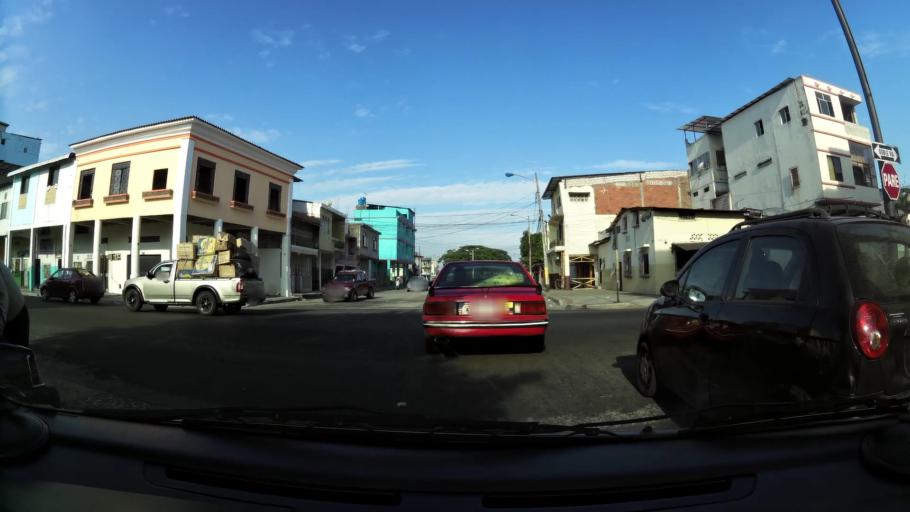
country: EC
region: Guayas
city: Guayaquil
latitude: -2.2094
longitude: -79.9040
